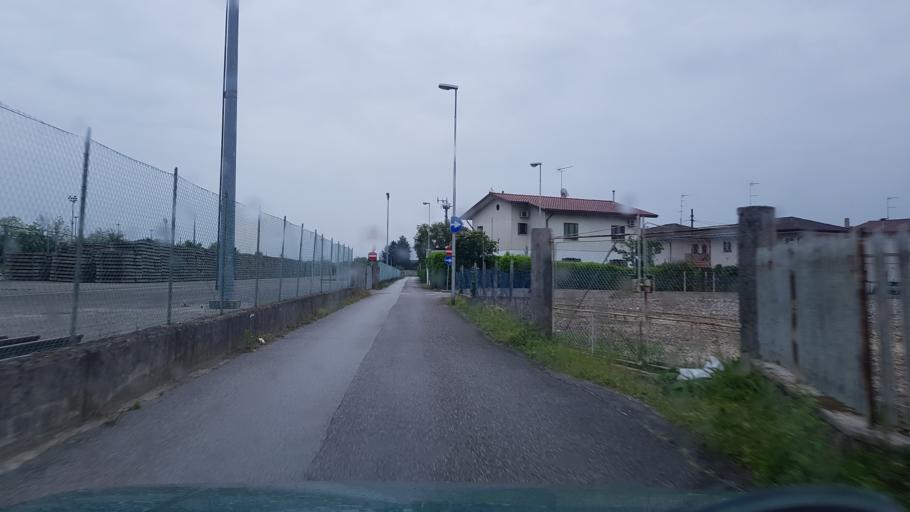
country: IT
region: Friuli Venezia Giulia
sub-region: Provincia di Udine
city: San Giovanni al Natisone
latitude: 45.9743
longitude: 13.3992
